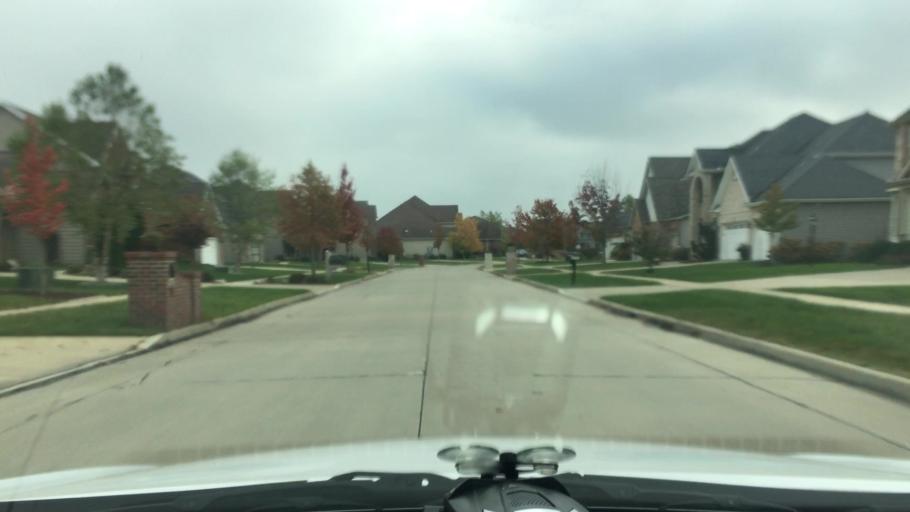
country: US
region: Illinois
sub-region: Champaign County
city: Savoy
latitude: 40.0947
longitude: -88.3257
